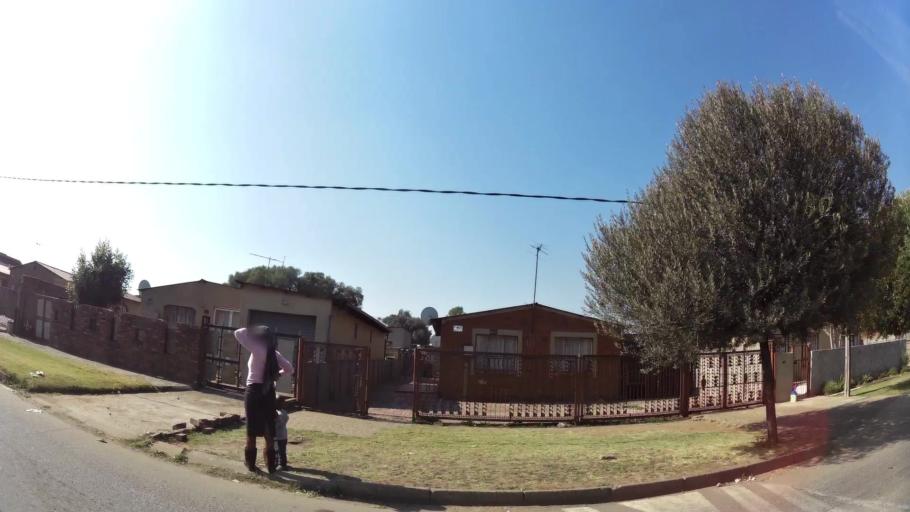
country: ZA
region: Gauteng
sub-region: Ekurhuleni Metropolitan Municipality
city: Boksburg
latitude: -26.2180
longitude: 28.2913
